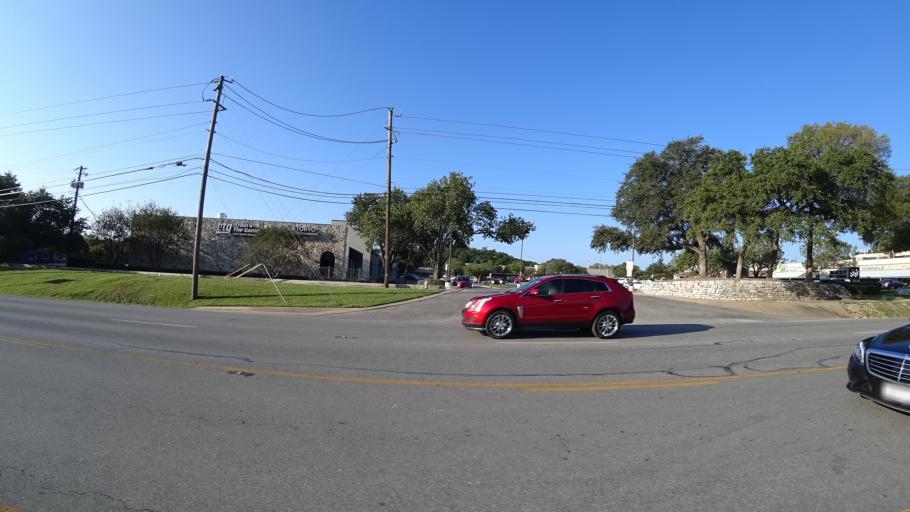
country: US
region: Texas
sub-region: Travis County
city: Rollingwood
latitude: 30.2735
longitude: -97.7990
